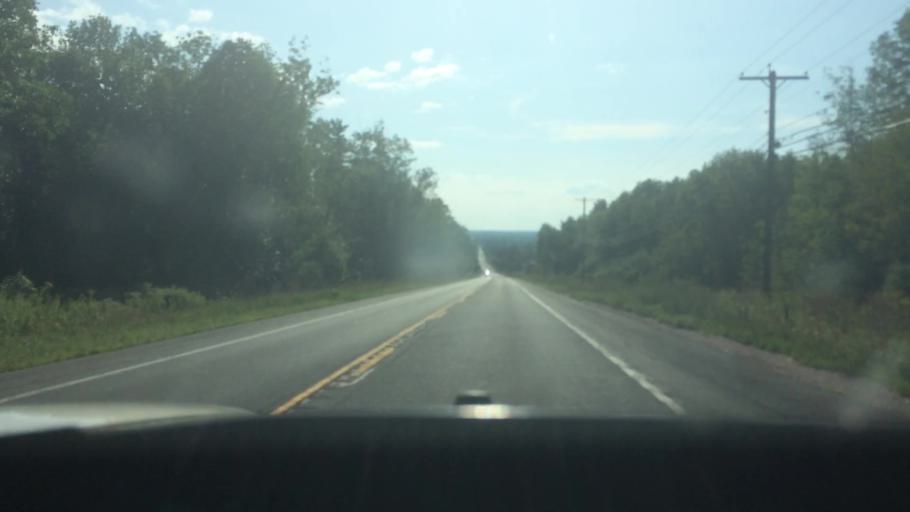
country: US
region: New York
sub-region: Franklin County
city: Malone
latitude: 44.8177
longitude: -74.3710
